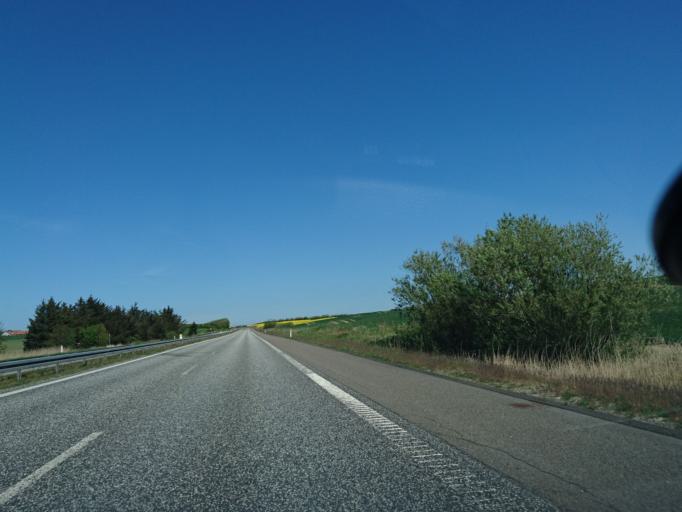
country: DK
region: North Denmark
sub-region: Hjorring Kommune
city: Hirtshals
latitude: 57.5510
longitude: 10.0087
